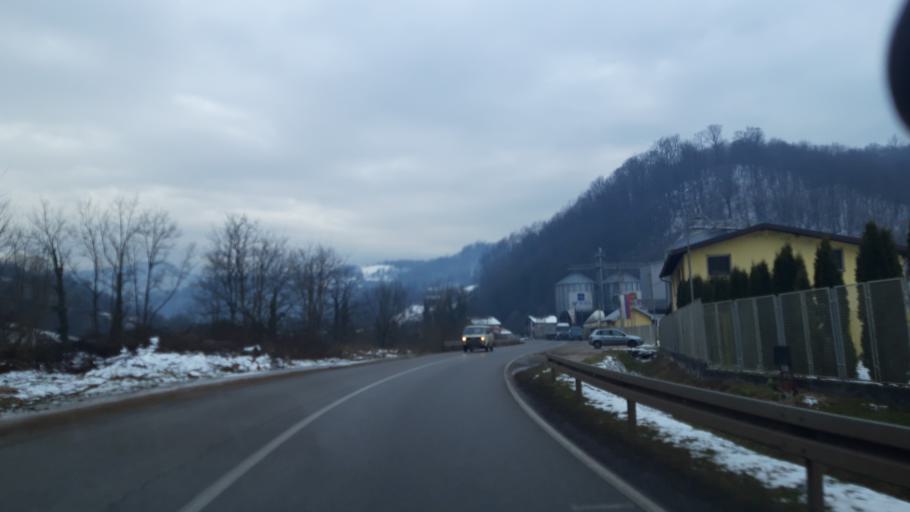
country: BA
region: Republika Srpska
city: Milici
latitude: 44.1850
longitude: 19.0767
